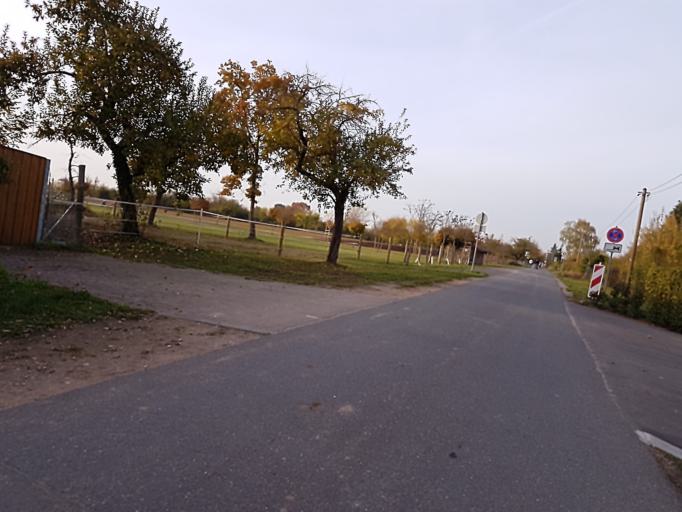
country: DE
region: Bavaria
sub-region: Regierungsbezirk Unterfranken
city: Niedernberg
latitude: 49.9026
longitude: 9.1419
